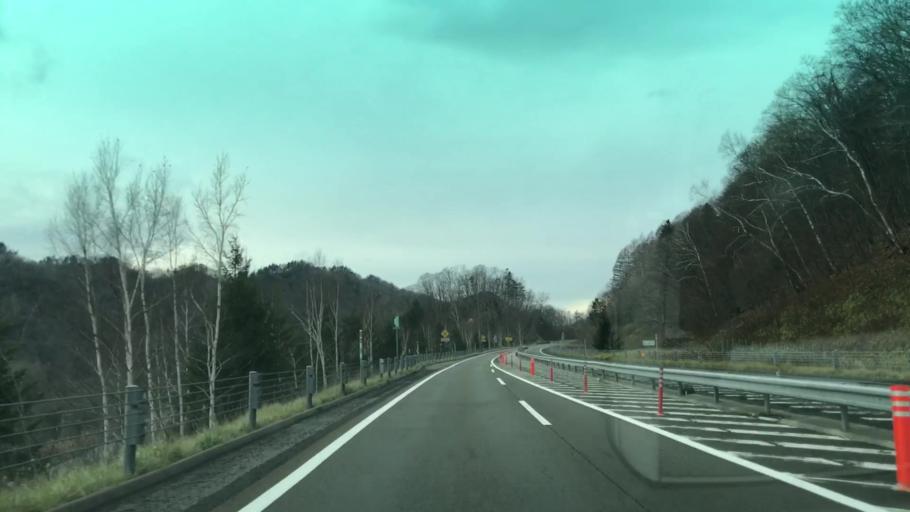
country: JP
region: Hokkaido
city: Chitose
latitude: 42.9081
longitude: 141.9884
